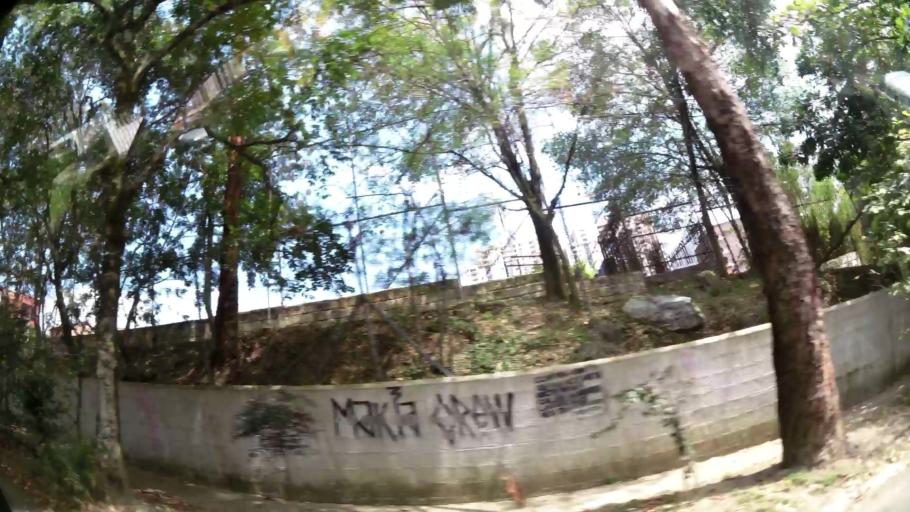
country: CO
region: Antioquia
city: Bello
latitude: 6.3126
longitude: -75.5594
